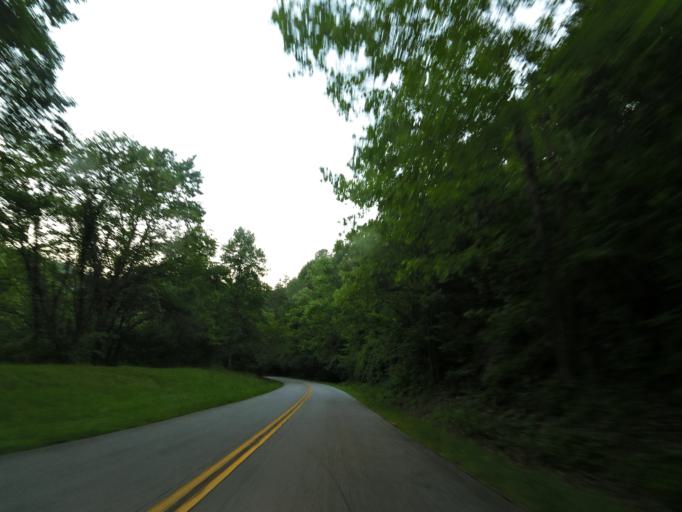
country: US
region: Tennessee
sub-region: Blount County
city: Maryville
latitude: 35.5719
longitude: -84.0033
